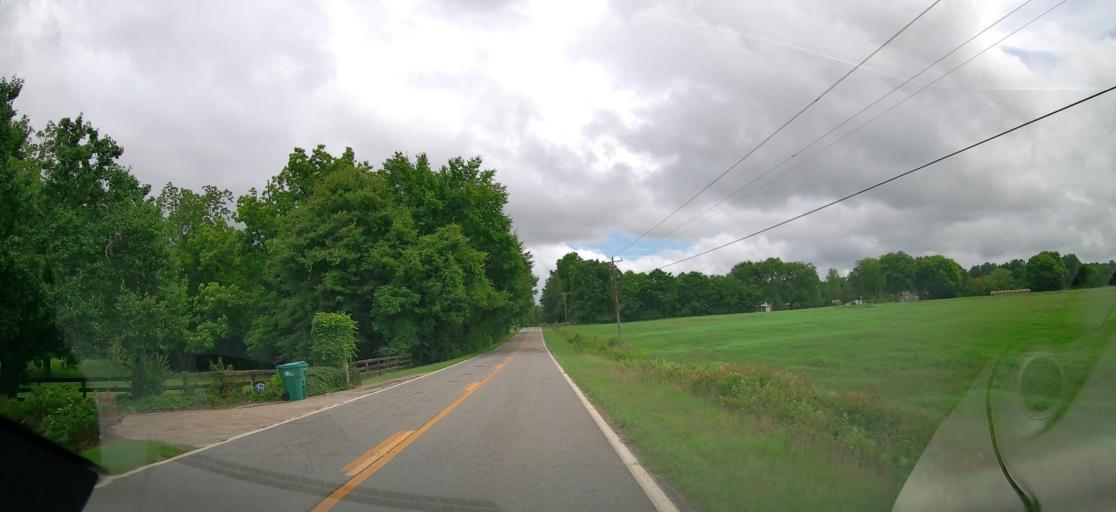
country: US
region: Georgia
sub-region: Bibb County
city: West Point
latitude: 32.7389
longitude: -83.7657
